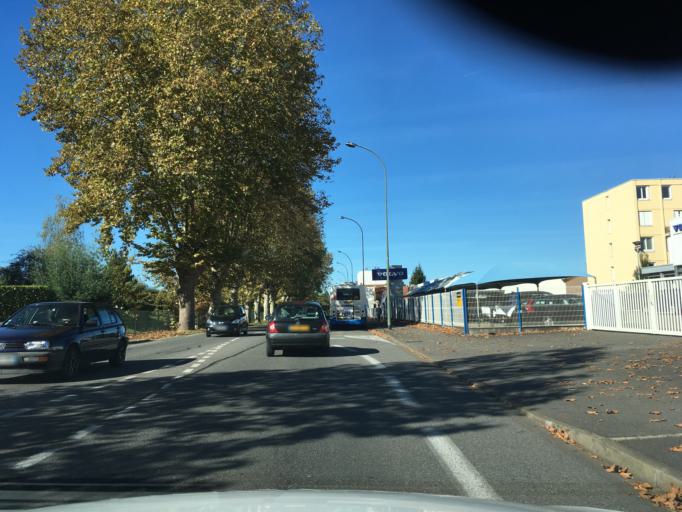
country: FR
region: Aquitaine
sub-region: Departement des Pyrenees-Atlantiques
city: Bizanos
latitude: 43.3072
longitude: -0.3355
